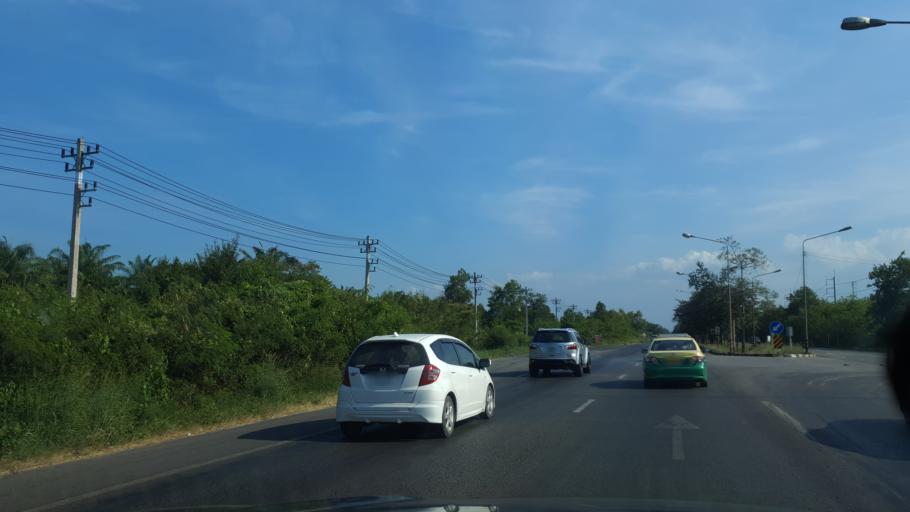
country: TH
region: Surat Thani
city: Phunphin
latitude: 9.0215
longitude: 99.1793
